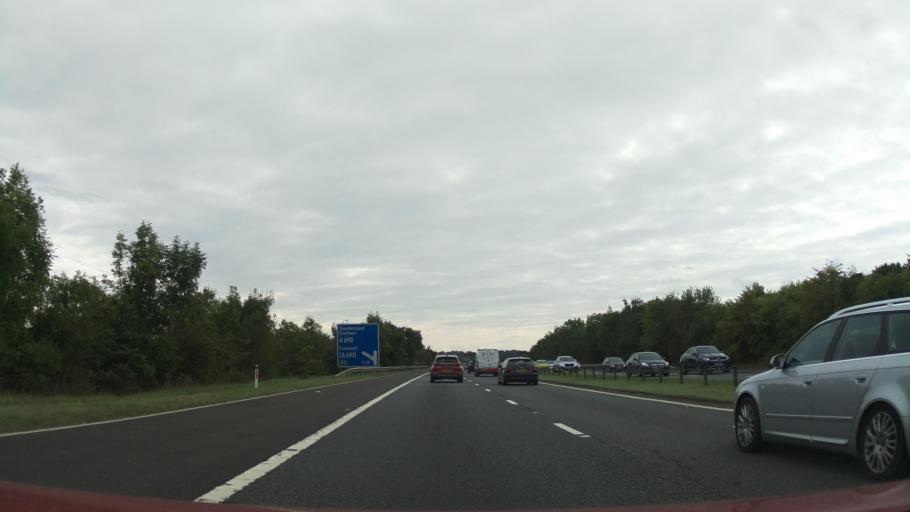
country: GB
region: England
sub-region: County Durham
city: West Rainton
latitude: 54.8064
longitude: -1.5226
